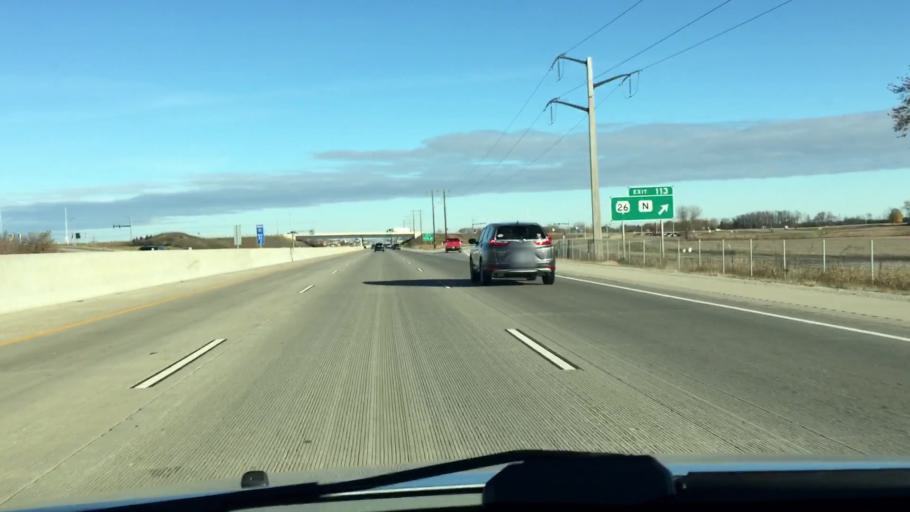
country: US
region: Wisconsin
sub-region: Winnebago County
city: Oshkosh
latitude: 43.9463
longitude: -88.5831
